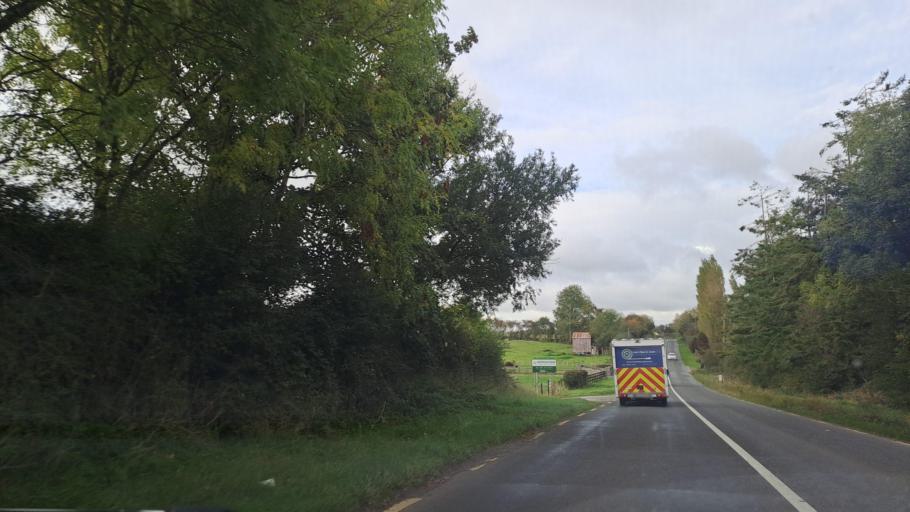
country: IE
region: Ulster
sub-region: An Cabhan
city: Kingscourt
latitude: 53.8031
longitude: -6.7370
